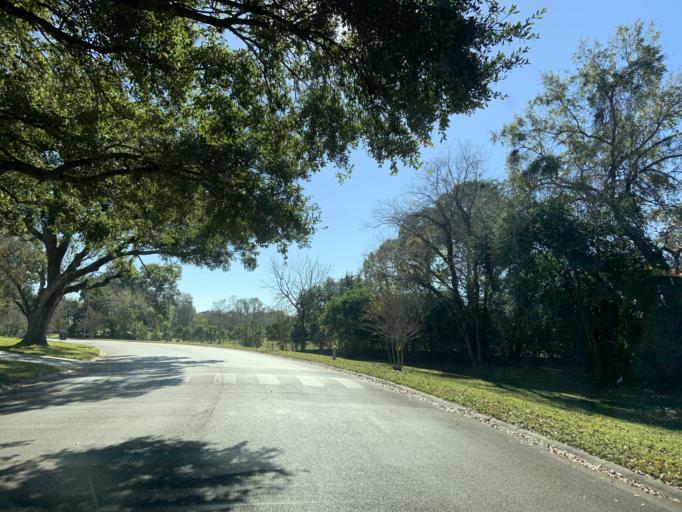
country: US
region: Texas
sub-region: Fort Bend County
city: Missouri City
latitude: 29.6782
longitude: -95.5178
